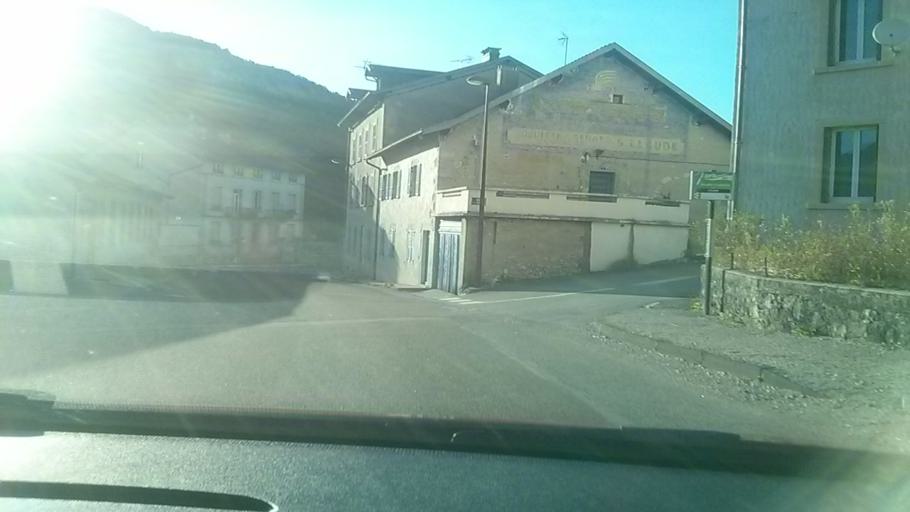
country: FR
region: Franche-Comte
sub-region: Departement du Jura
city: Saint-Claude
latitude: 46.3716
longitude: 5.8746
